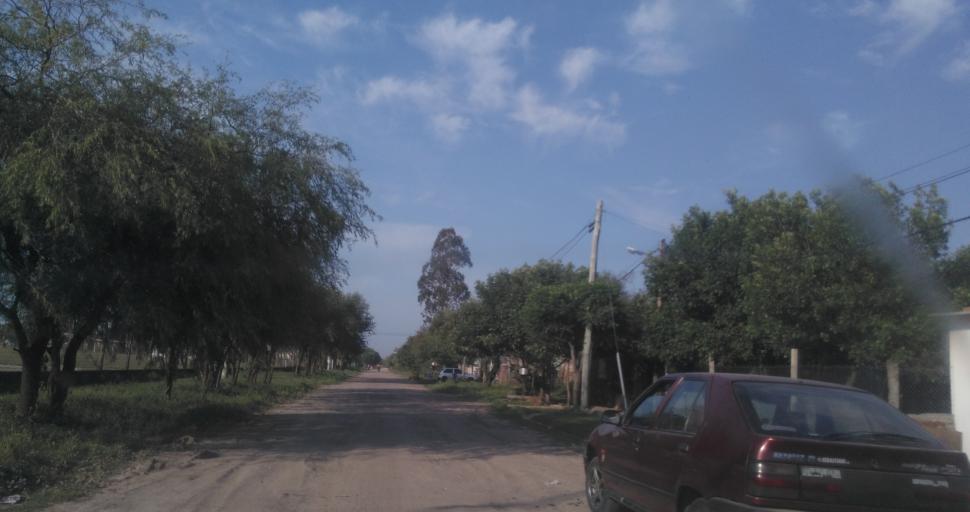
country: AR
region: Chaco
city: Resistencia
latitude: -27.4799
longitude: -59.0026
